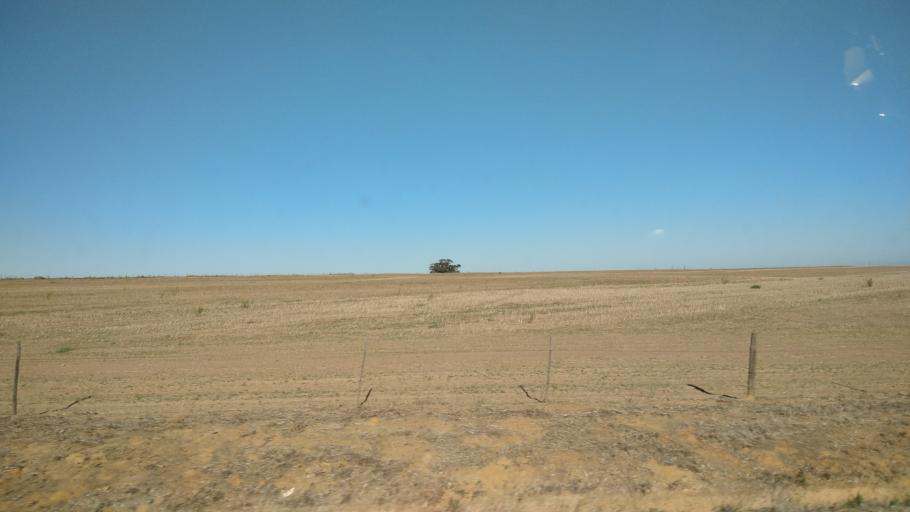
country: ZA
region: Western Cape
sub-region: West Coast District Municipality
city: Malmesbury
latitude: -33.3572
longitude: 18.6448
